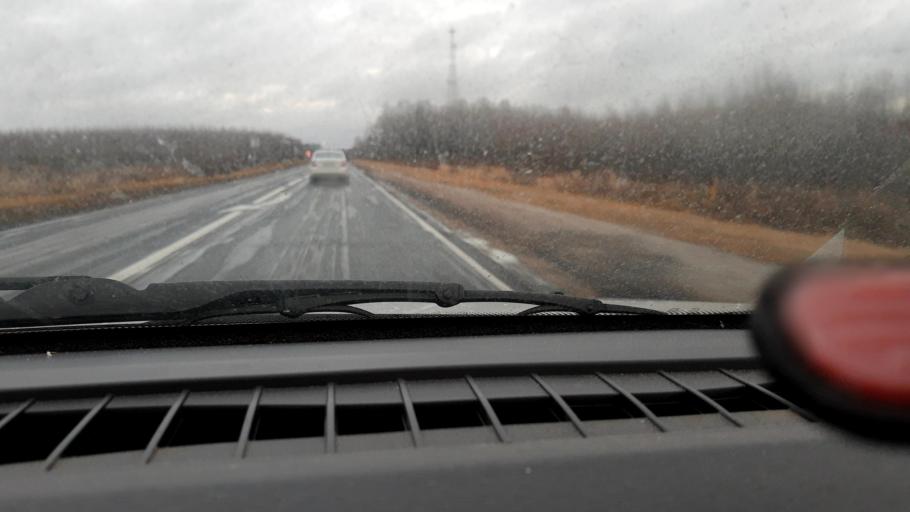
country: RU
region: Nizjnij Novgorod
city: Krasnyye Baki
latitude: 57.0951
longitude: 45.1529
